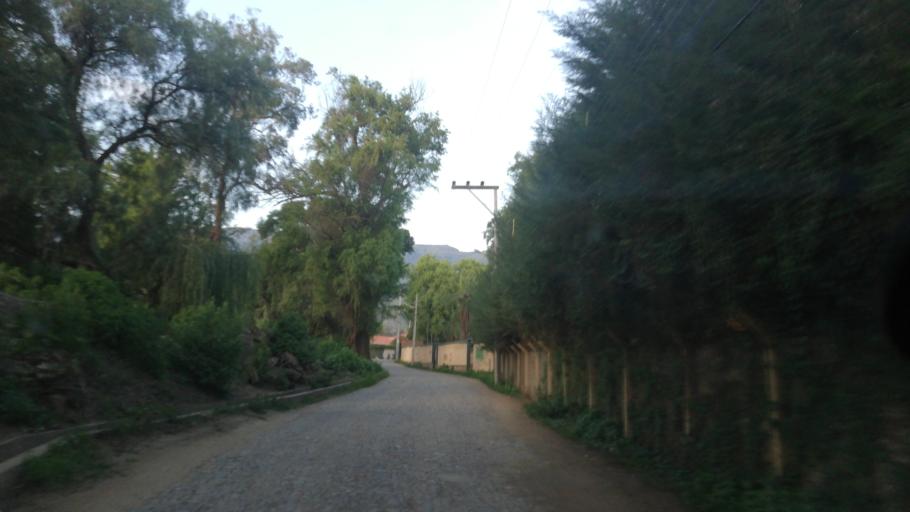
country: BO
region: Cochabamba
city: Cochabamba
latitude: -17.3482
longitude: -66.2136
